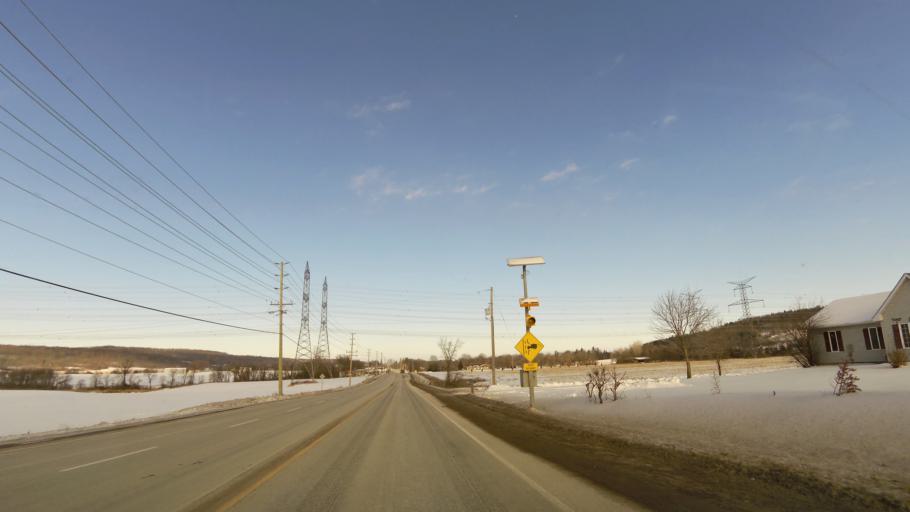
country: CA
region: Ontario
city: Quinte West
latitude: 44.1505
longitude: -77.7956
